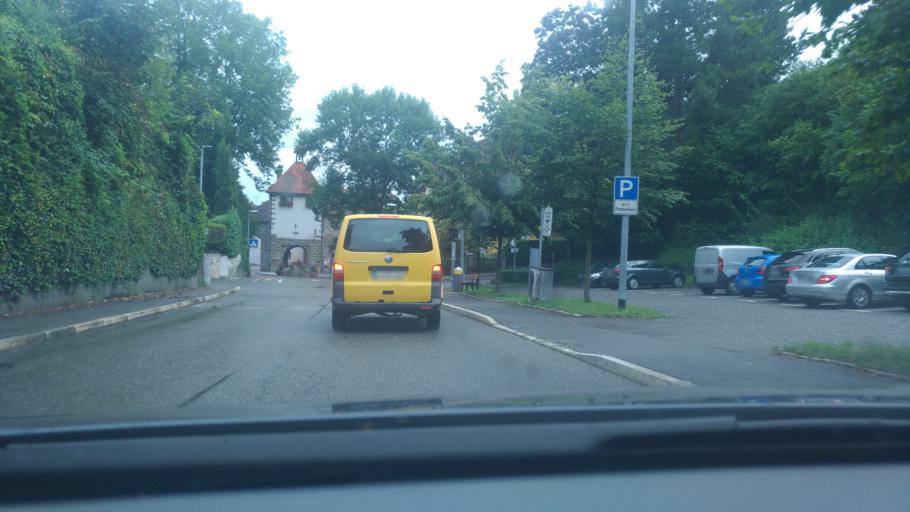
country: DE
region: Baden-Wuerttemberg
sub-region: Tuebingen Region
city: Uberlingen
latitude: 47.7714
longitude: 9.1566
